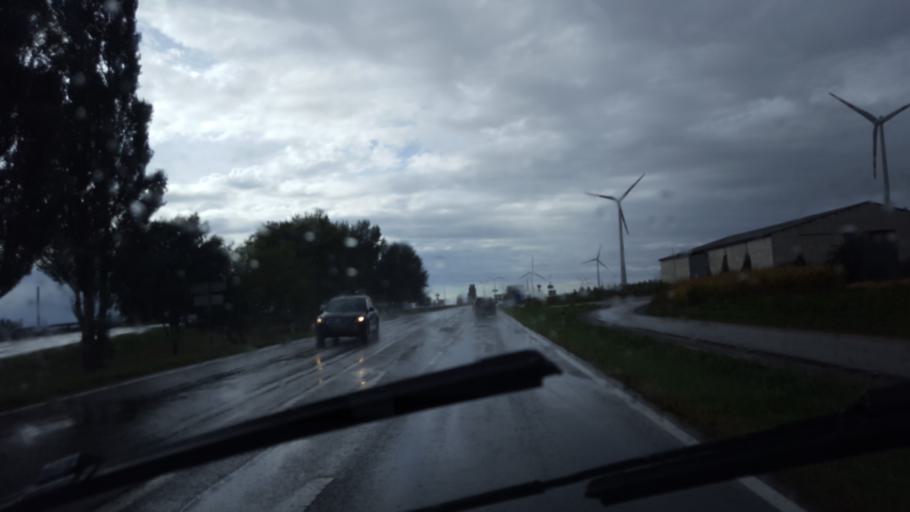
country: AT
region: Lower Austria
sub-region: Politischer Bezirk Bruck an der Leitha
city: Bruck an der Leitha
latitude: 48.0255
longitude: 16.7441
